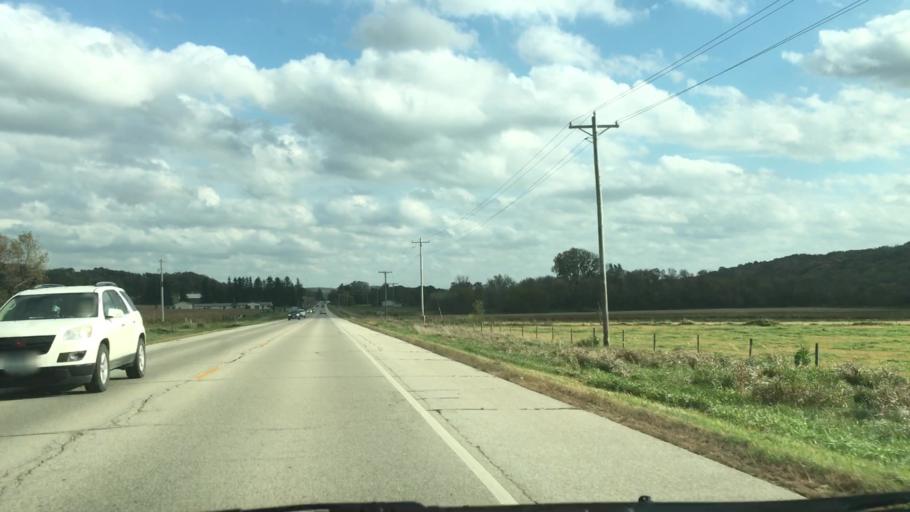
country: US
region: Minnesota
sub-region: Fillmore County
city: Chatfield
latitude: 43.8768
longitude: -92.2153
